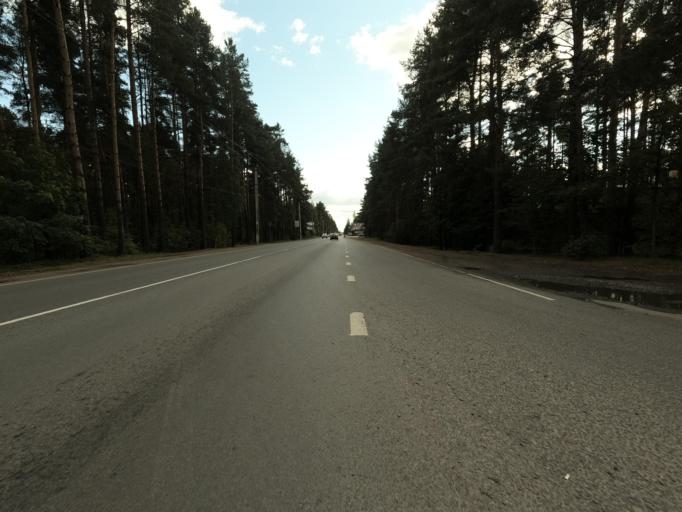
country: RU
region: Leningrad
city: Vsevolozhsk
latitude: 60.0018
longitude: 30.6624
